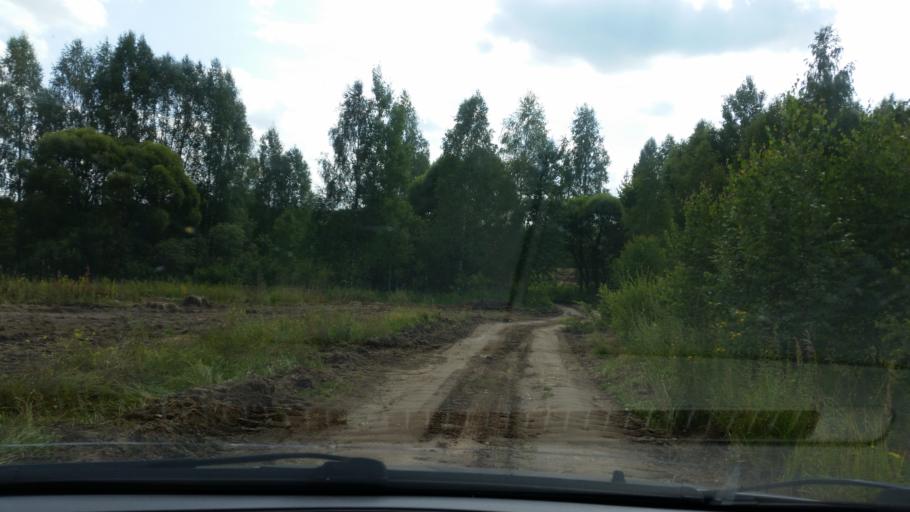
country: RU
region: Moskovskaya
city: Pushchino
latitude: 54.9309
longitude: 37.7043
